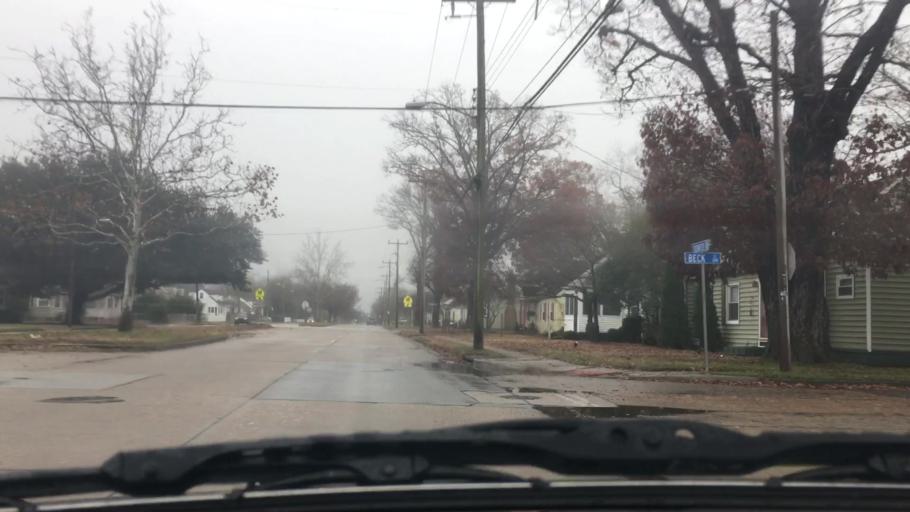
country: US
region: Virginia
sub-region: City of Norfolk
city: Norfolk
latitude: 36.9372
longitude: -76.2545
